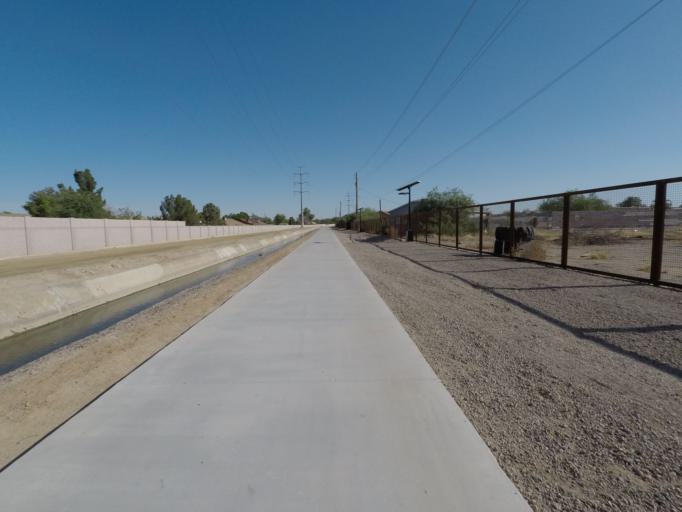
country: US
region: Arizona
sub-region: Maricopa County
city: Guadalupe
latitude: 33.3599
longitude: -111.9564
